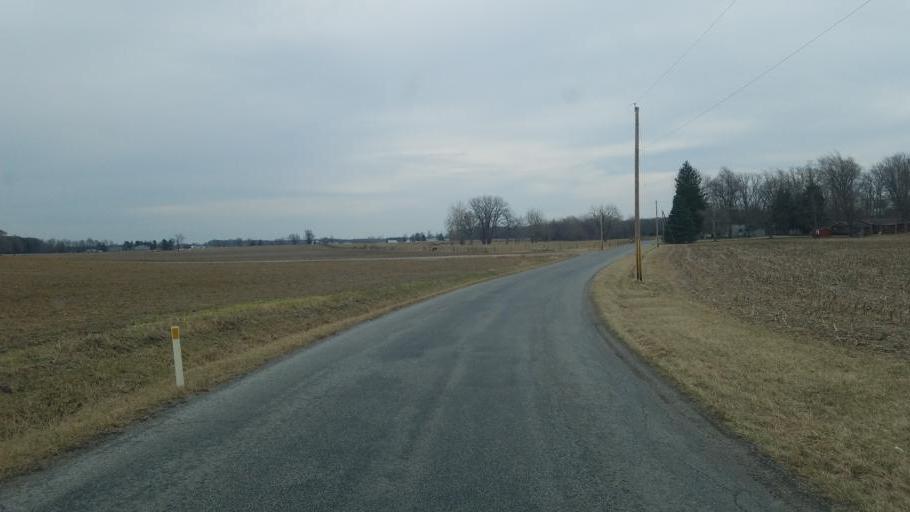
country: US
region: Ohio
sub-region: Richland County
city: Shelby
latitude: 40.8363
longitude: -82.6475
